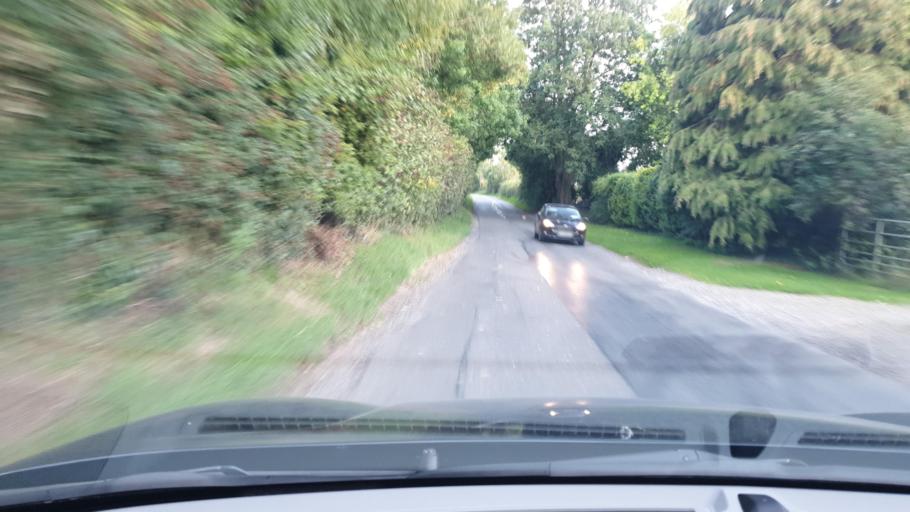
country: IE
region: Leinster
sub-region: An Mhi
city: Ashbourne
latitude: 53.5403
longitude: -6.3415
